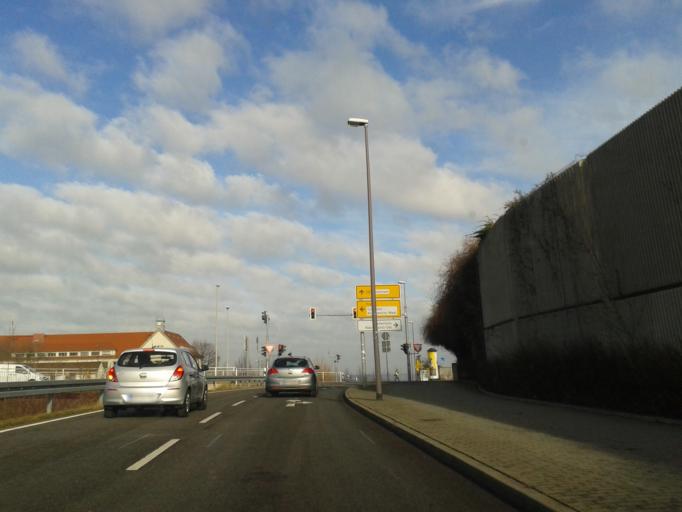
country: DE
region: Saxony
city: Bannewitz
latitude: 51.0191
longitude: 13.7296
